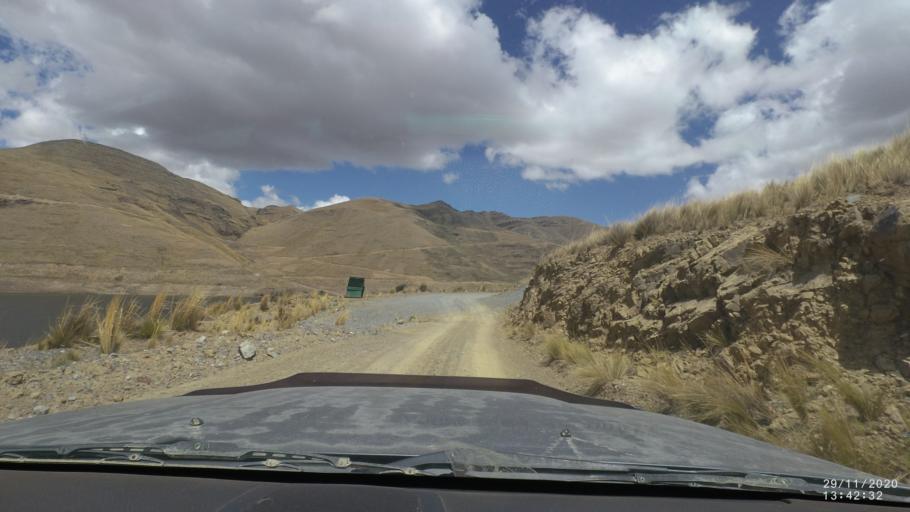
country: BO
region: Cochabamba
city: Cochabamba
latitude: -17.1364
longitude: -66.3228
